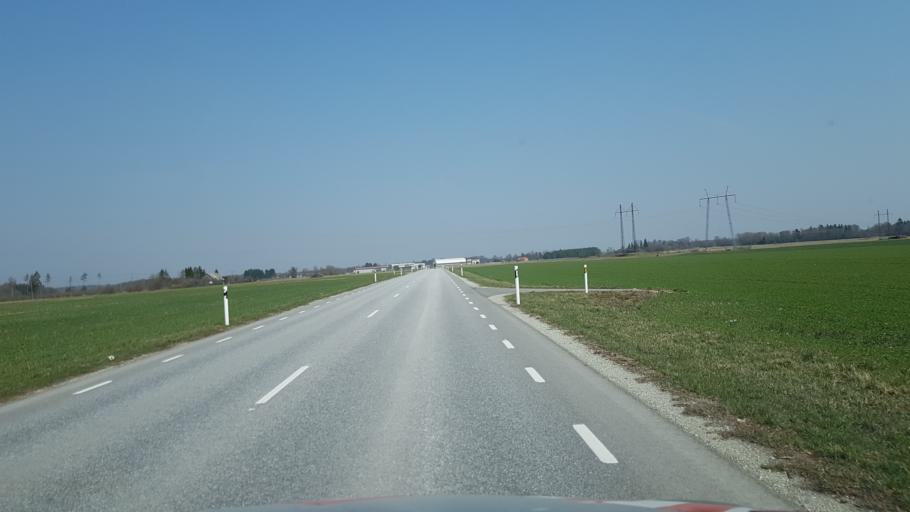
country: EE
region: Harju
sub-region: Saku vald
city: Saku
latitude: 59.2605
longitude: 24.7149
